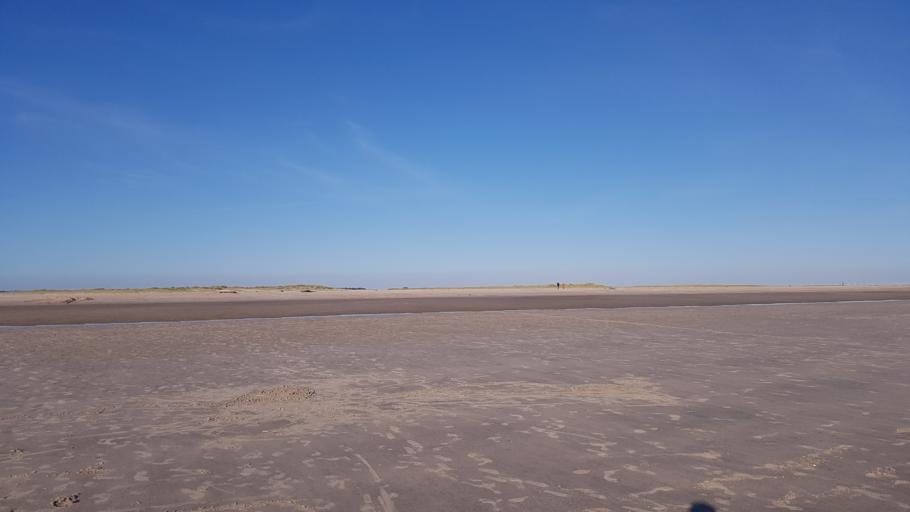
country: DE
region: Schleswig-Holstein
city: List
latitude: 55.0719
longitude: 8.4899
